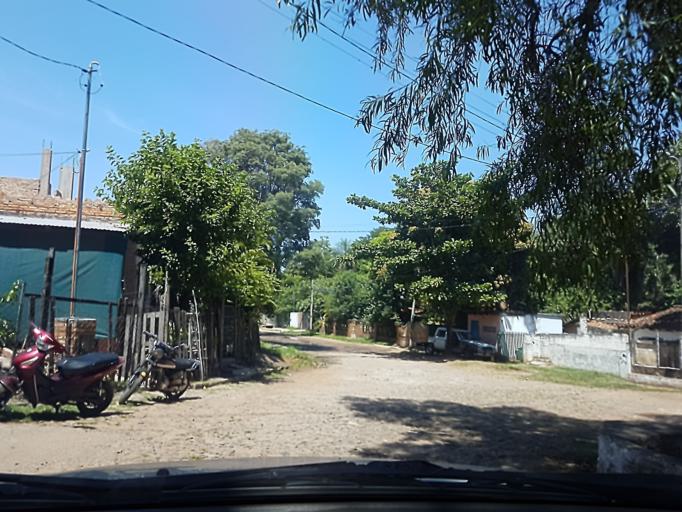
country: PY
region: Central
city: Fernando de la Mora
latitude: -25.2929
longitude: -57.5355
